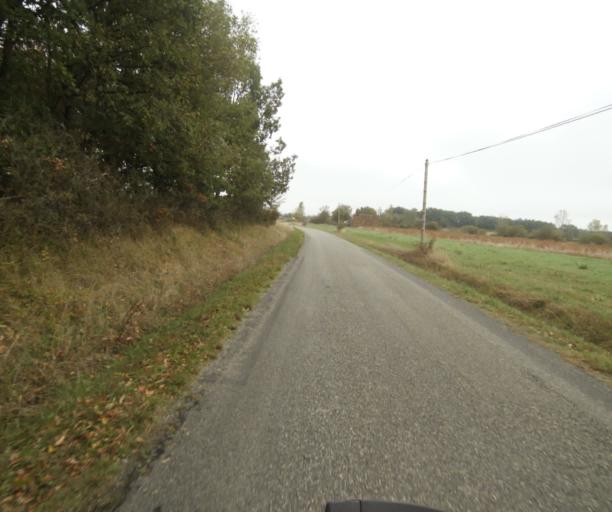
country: FR
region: Midi-Pyrenees
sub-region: Departement du Tarn-et-Garonne
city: Orgueil
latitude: 43.8958
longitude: 1.3910
